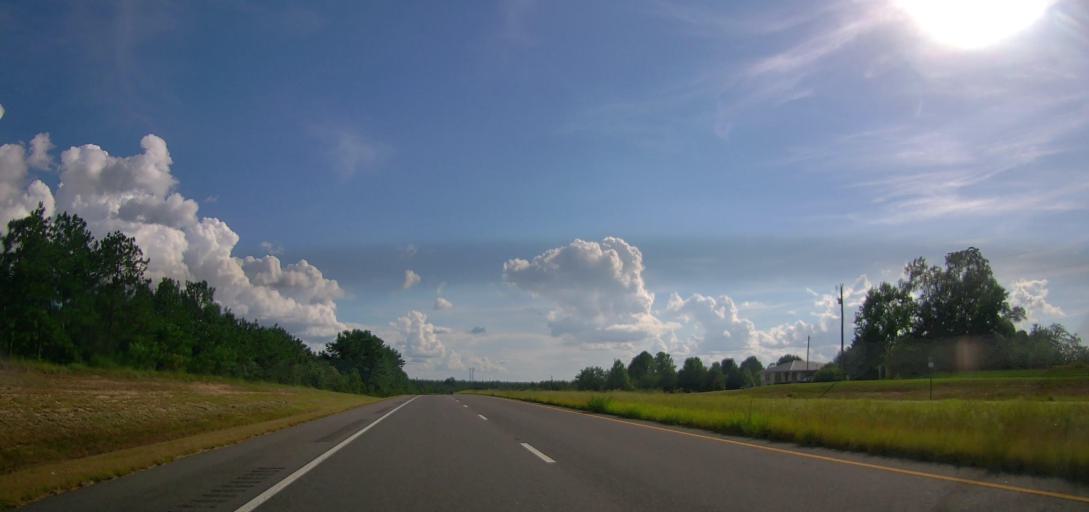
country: US
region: Georgia
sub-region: Talbot County
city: Talbotton
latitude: 32.5967
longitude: -84.4920
